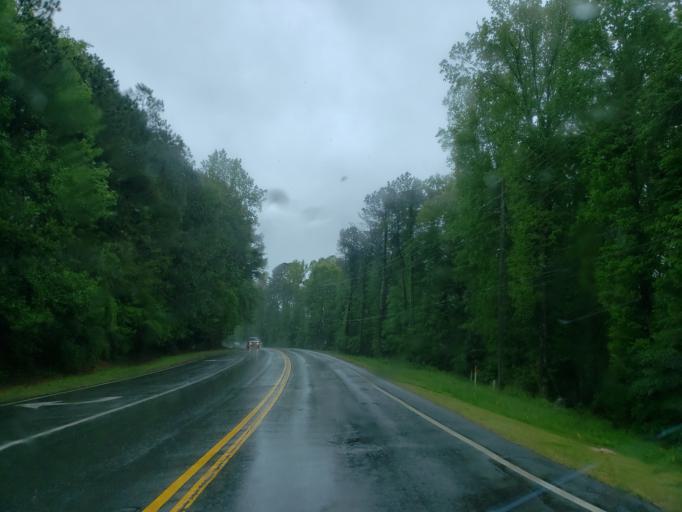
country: US
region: Georgia
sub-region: Carroll County
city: Villa Rica
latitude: 33.7357
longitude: -84.9729
